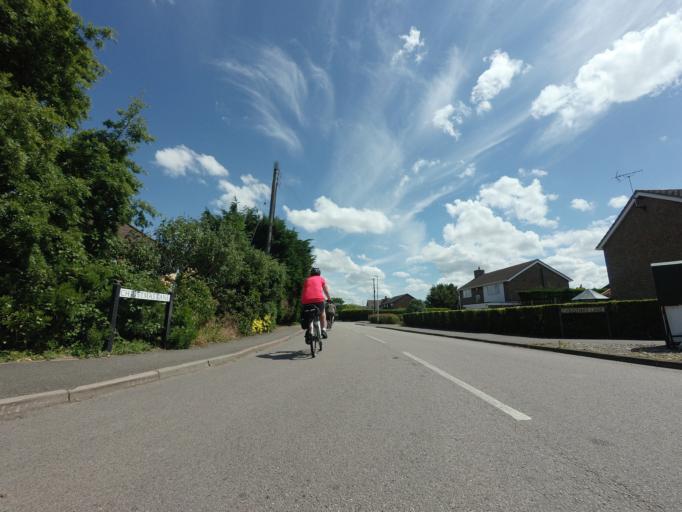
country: GB
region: England
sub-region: Medway
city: High Halstow
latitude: 51.4484
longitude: 0.5610
